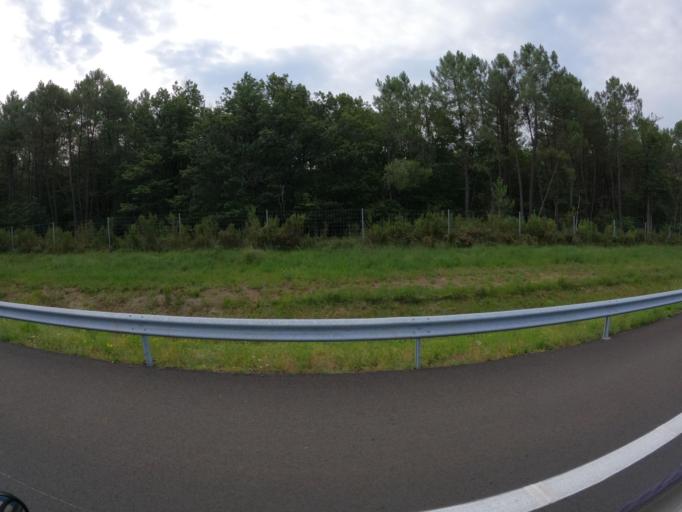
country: FR
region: Centre
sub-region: Departement d'Indre-et-Loire
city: Langeais
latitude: 47.3416
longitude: 0.3554
